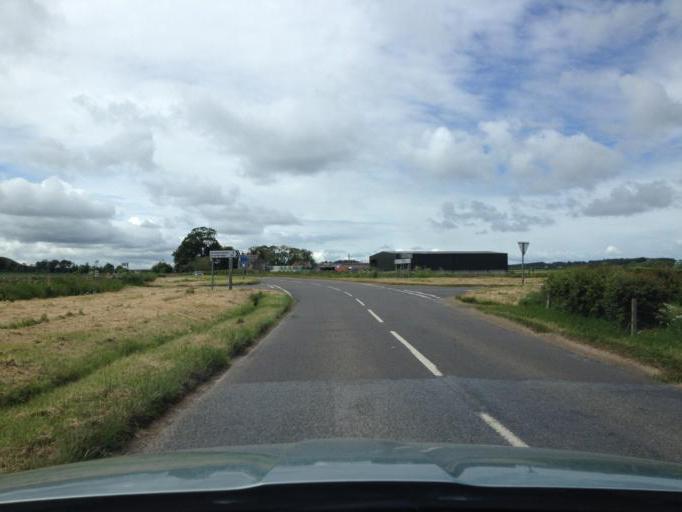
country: GB
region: Scotland
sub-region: Fife
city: Strathkinness
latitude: 56.3206
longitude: -2.8710
